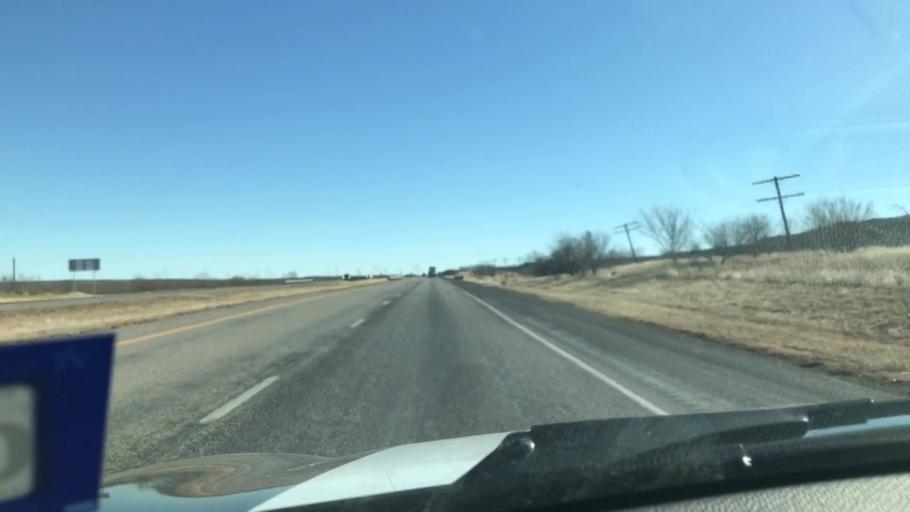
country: US
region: Texas
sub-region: Scurry County
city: Snyder
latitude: 32.9670
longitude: -101.0961
